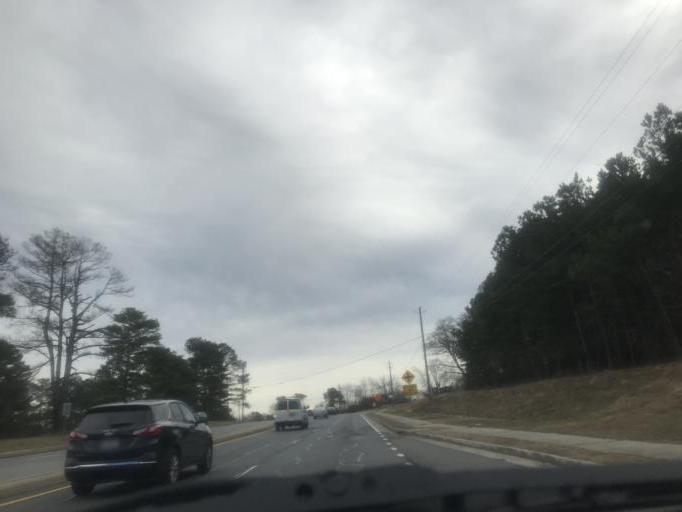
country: US
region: Georgia
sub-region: Gwinnett County
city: Buford
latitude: 34.0689
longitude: -83.9582
